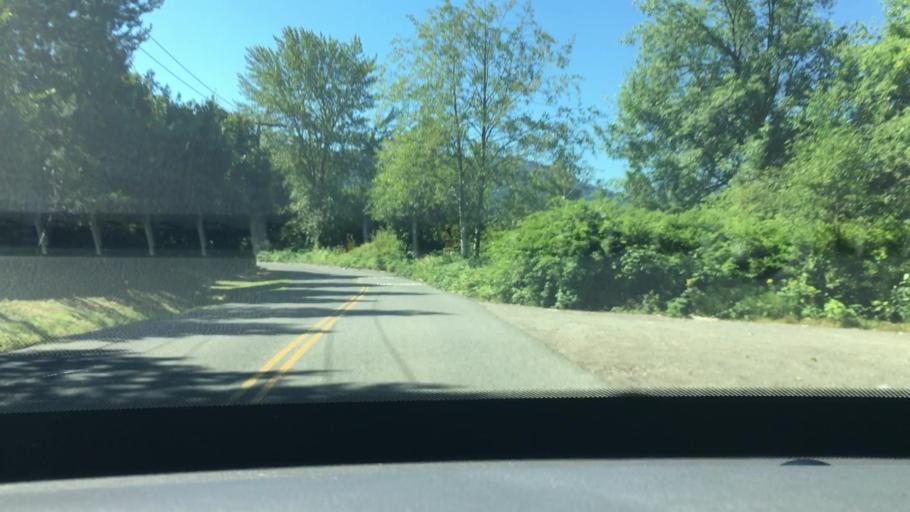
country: US
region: Washington
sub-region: King County
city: Issaquah
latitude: 47.5491
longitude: -122.0574
